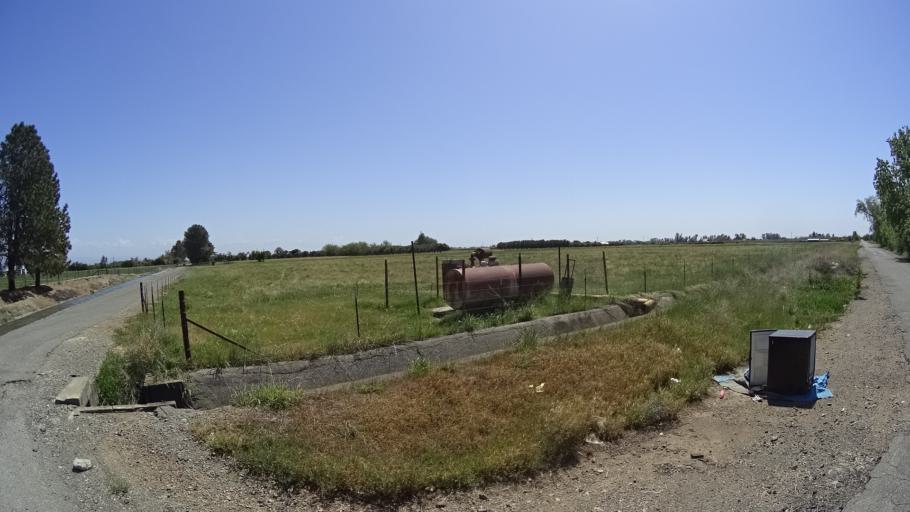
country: US
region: California
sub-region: Glenn County
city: Orland
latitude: 39.7832
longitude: -122.1835
